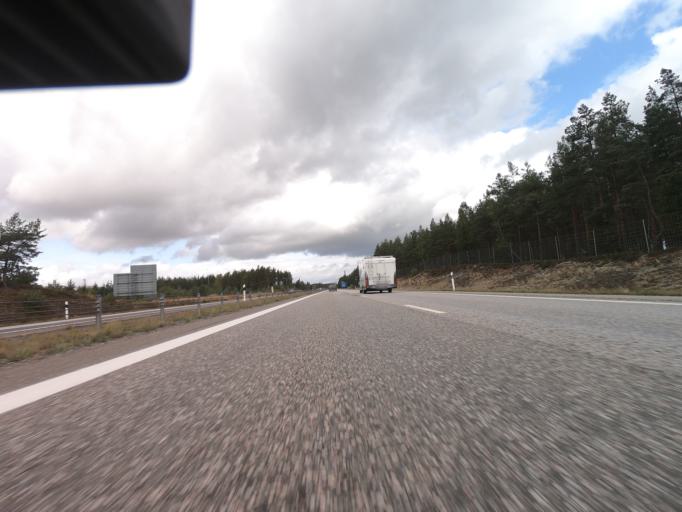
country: SE
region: Joenkoeping
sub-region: Jonkopings Kommun
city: Odensjo
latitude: 57.6811
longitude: 14.1657
